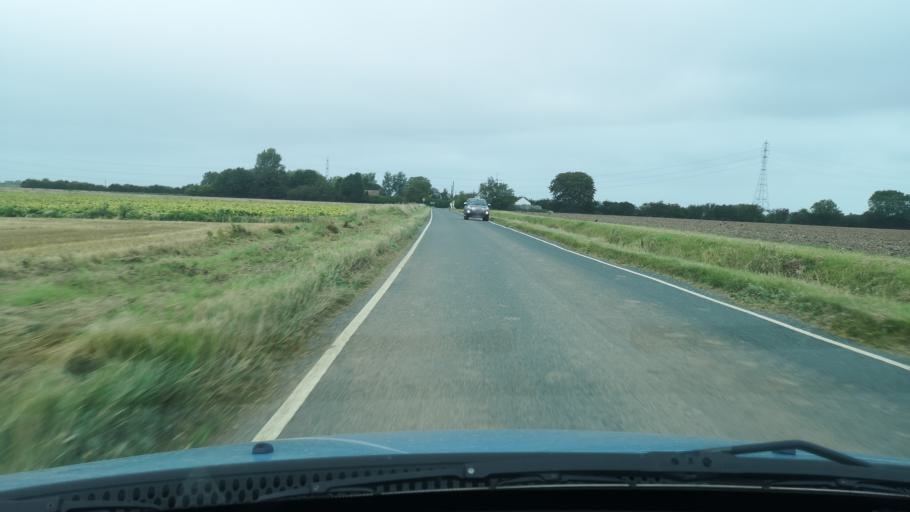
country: GB
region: England
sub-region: North Lincolnshire
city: Burton upon Stather
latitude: 53.6977
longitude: -0.7322
